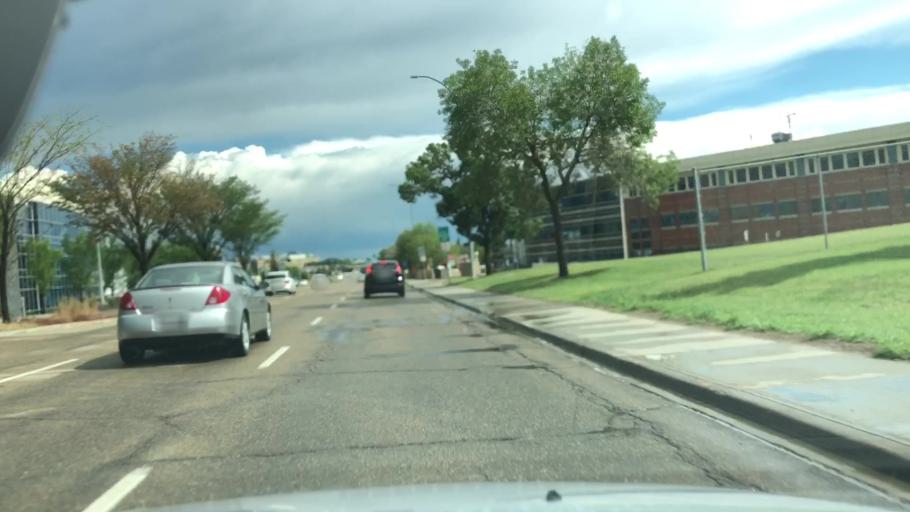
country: CA
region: Alberta
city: Edmonton
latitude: 53.5618
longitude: -113.5109
